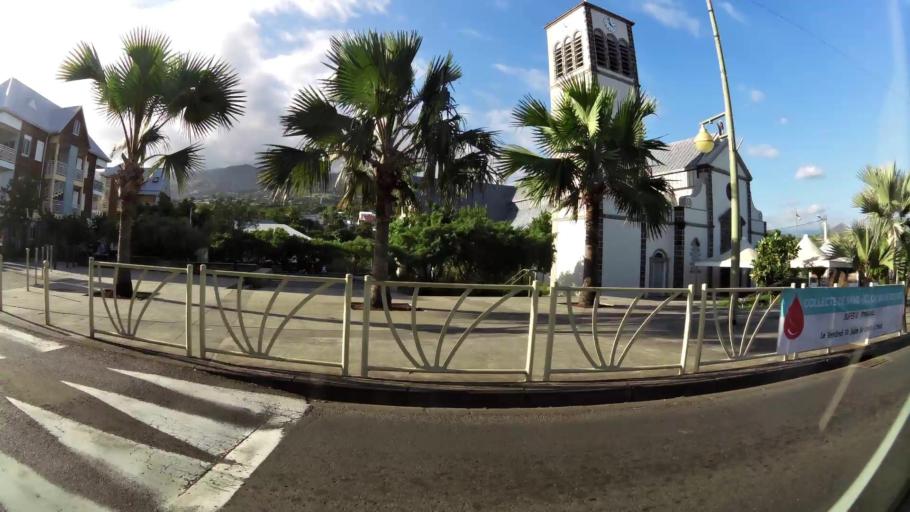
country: RE
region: Reunion
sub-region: Reunion
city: Les Avirons
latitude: -21.2654
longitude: 55.3667
